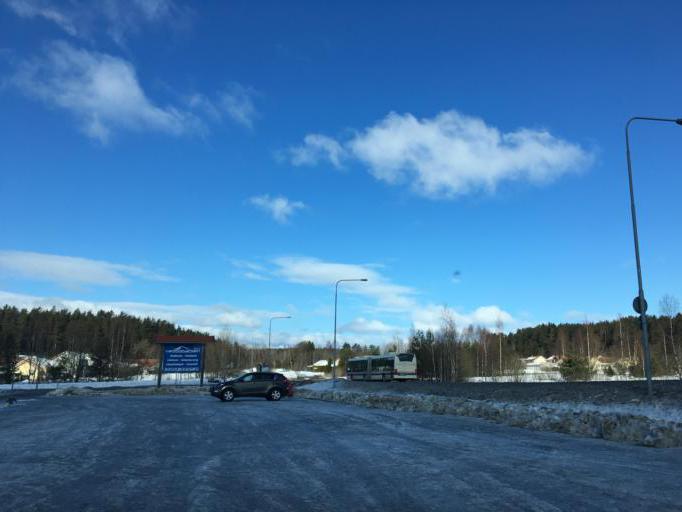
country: SE
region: Vaestmanland
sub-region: Vasteras
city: Vasteras
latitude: 59.6261
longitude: 16.4843
